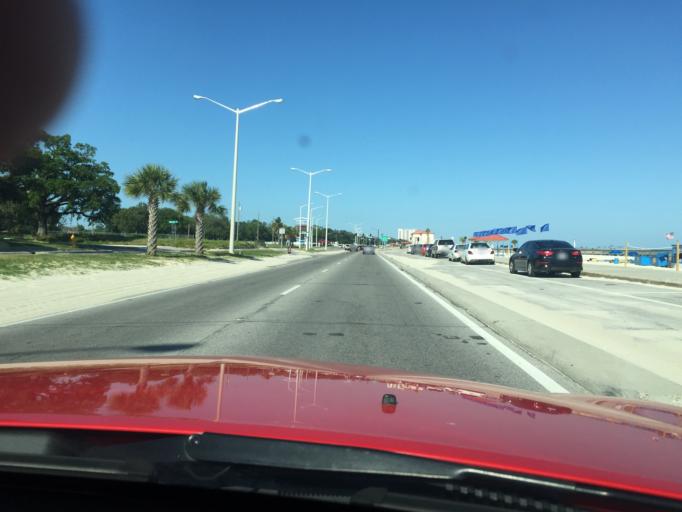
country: US
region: Mississippi
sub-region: Harrison County
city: Biloxi
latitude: 30.3905
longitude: -88.9778
